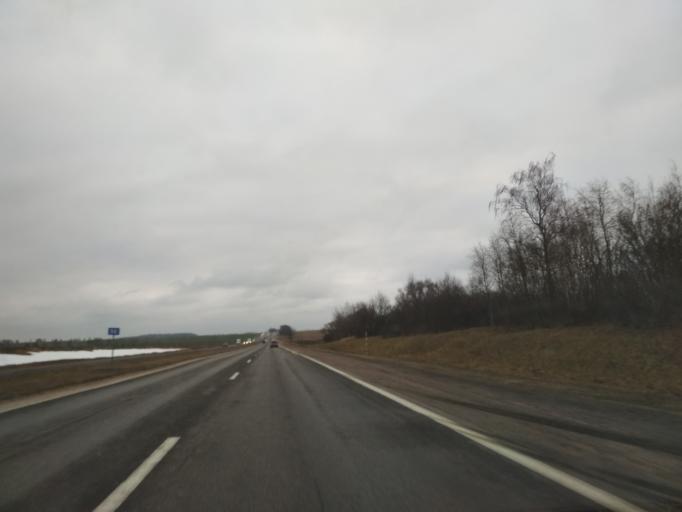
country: BY
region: Minsk
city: Blon'
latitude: 53.5617
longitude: 28.1465
